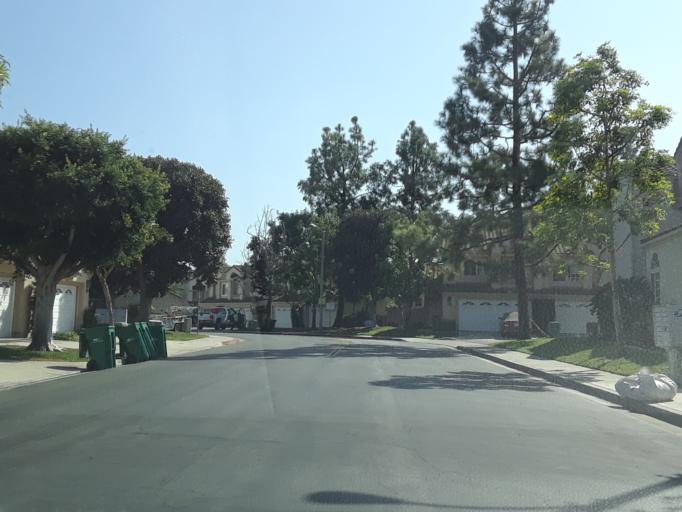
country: US
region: California
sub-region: Orange County
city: Irvine
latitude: 33.6748
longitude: -117.8304
